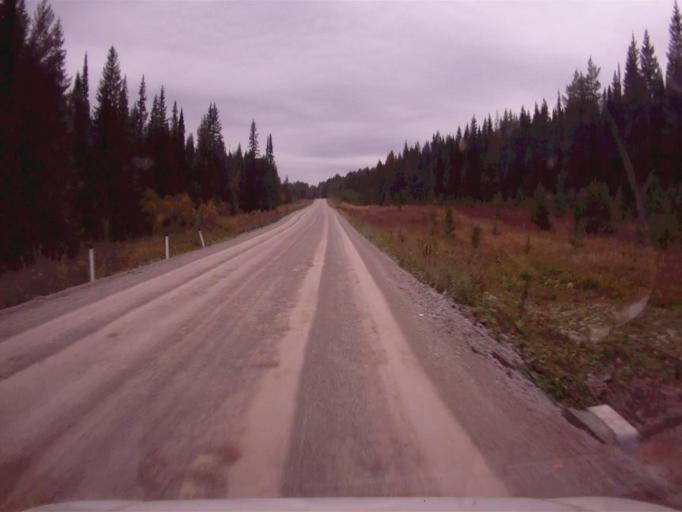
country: RU
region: Chelyabinsk
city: Nyazepetrovsk
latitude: 56.0548
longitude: 59.5449
